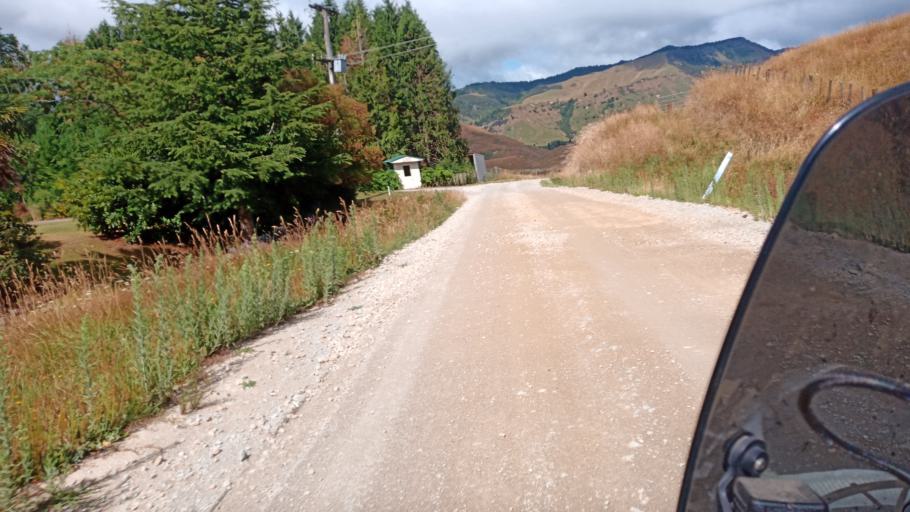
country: NZ
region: Hawke's Bay
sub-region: Wairoa District
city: Wairoa
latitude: -38.6098
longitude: 177.4454
